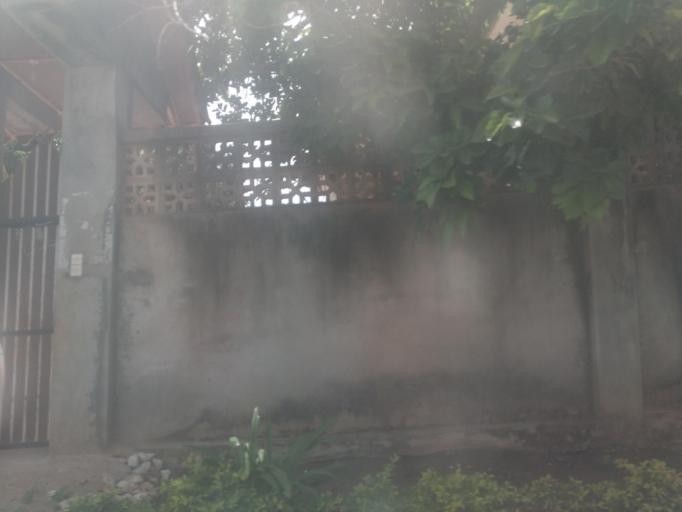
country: TZ
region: Zanzibar Urban/West
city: Zanzibar
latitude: -6.2145
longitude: 39.2057
